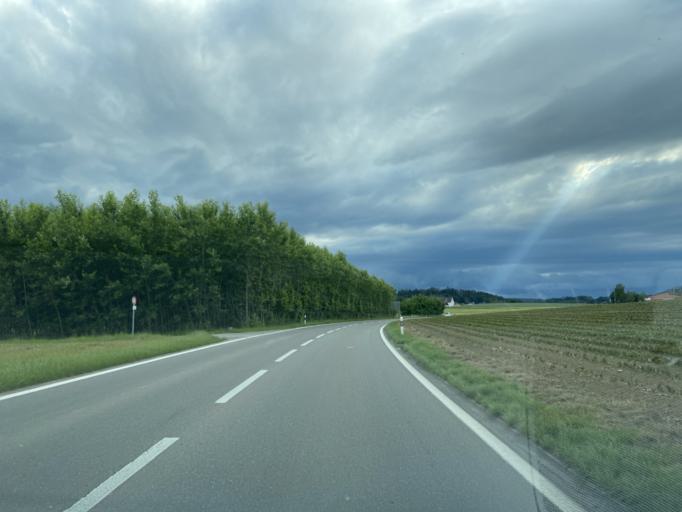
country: CH
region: Thurgau
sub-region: Frauenfeld District
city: Matzingen
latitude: 47.5068
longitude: 8.9289
